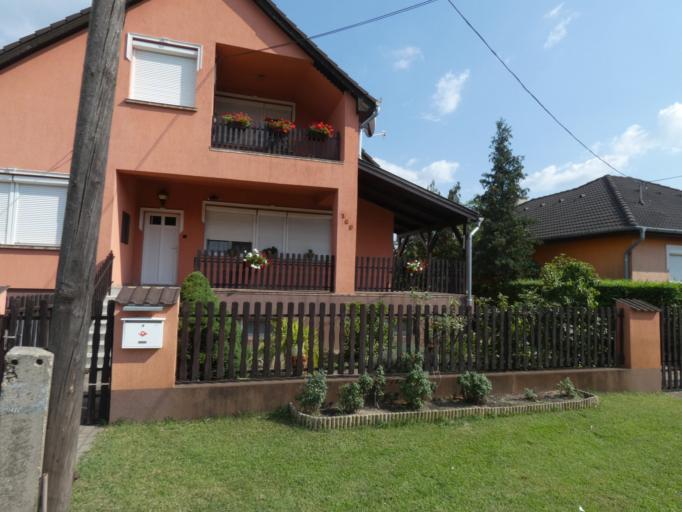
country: HU
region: Pest
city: Taborfalva
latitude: 47.1157
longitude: 19.4958
